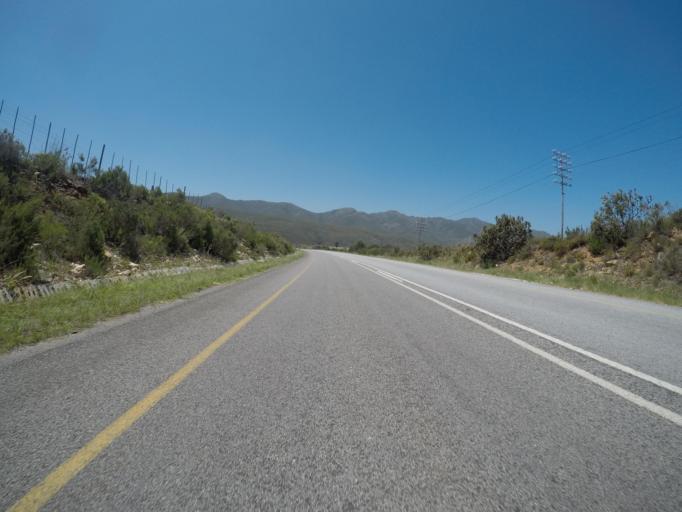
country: ZA
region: Eastern Cape
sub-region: Cacadu District Municipality
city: Kareedouw
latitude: -33.9488
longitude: 24.3030
